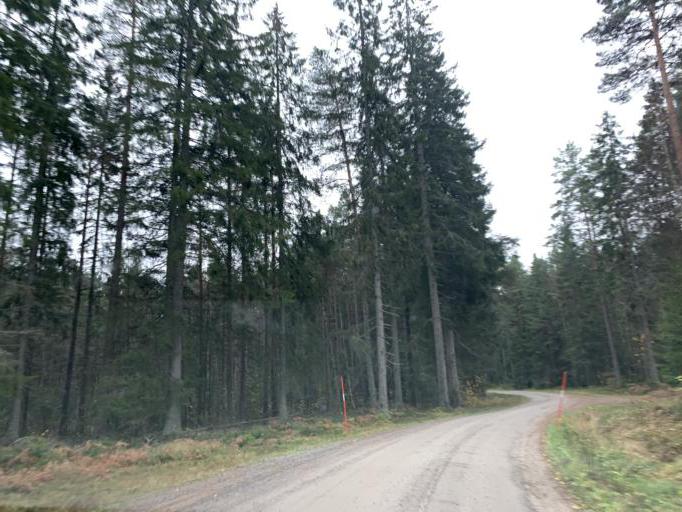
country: SE
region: Vaestmanland
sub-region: Kopings Kommun
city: Koping
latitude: 59.6229
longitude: 16.0684
